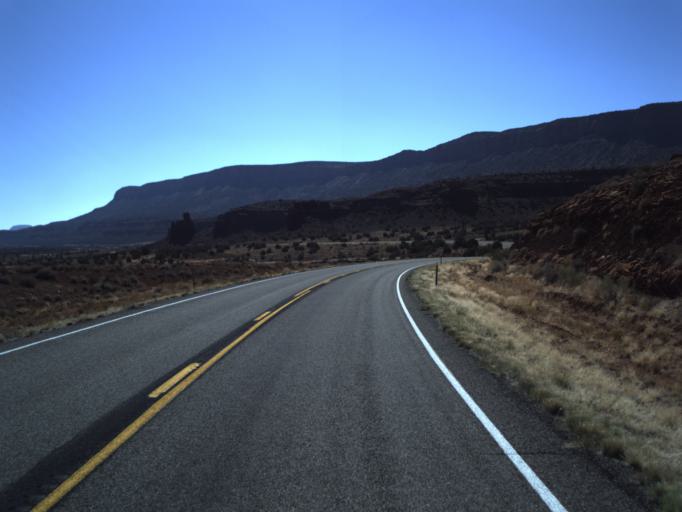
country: US
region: Utah
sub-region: San Juan County
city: Blanding
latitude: 37.7112
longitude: -110.2427
